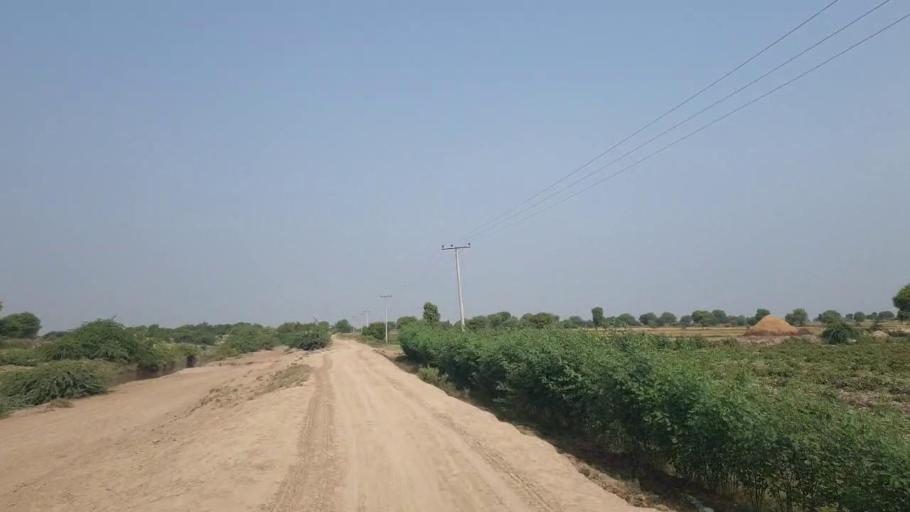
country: PK
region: Sindh
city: Badin
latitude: 24.6960
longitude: 68.7785
